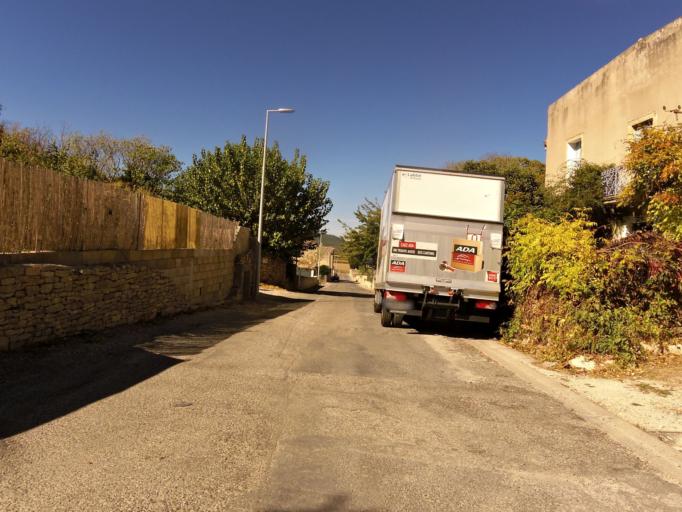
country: FR
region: Languedoc-Roussillon
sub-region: Departement du Gard
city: Nages-et-Solorgues
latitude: 43.7742
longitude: 4.2320
